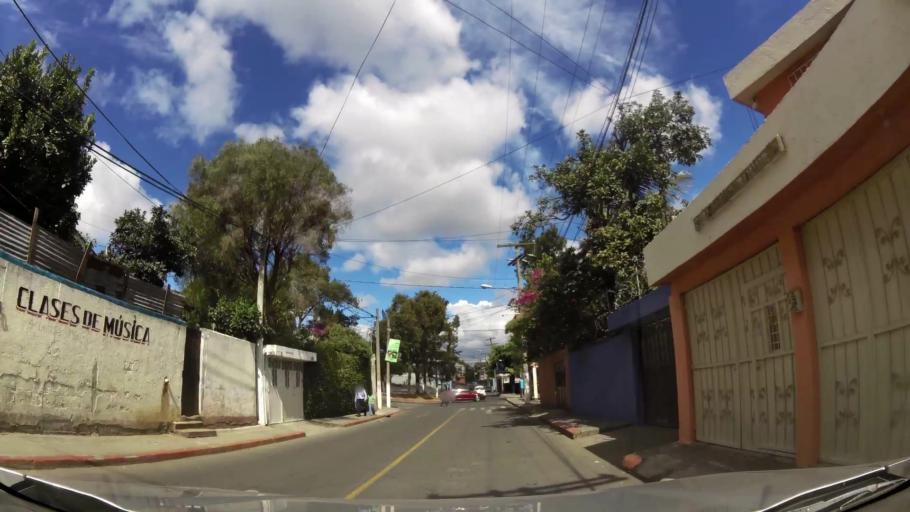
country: GT
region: Guatemala
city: Villa Nueva
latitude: 14.5499
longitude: -90.5467
